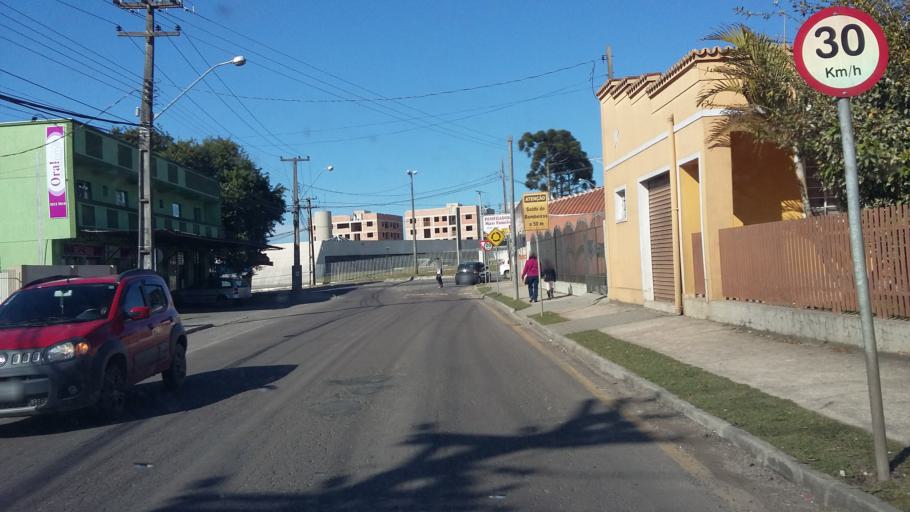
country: BR
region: Parana
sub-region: Campo Largo
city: Campo Largo
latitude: -25.4535
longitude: -49.5415
